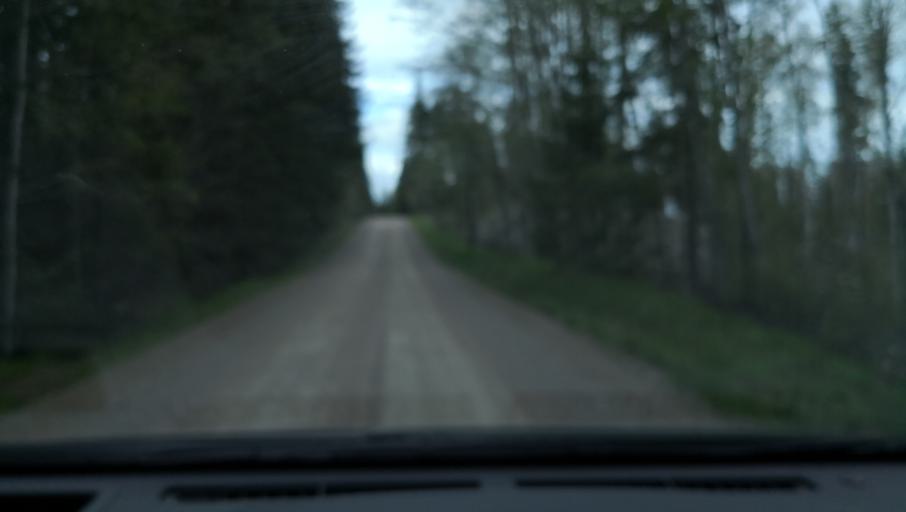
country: SE
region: Vaestmanland
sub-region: Fagersta Kommun
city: Fagersta
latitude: 60.1087
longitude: 15.7971
